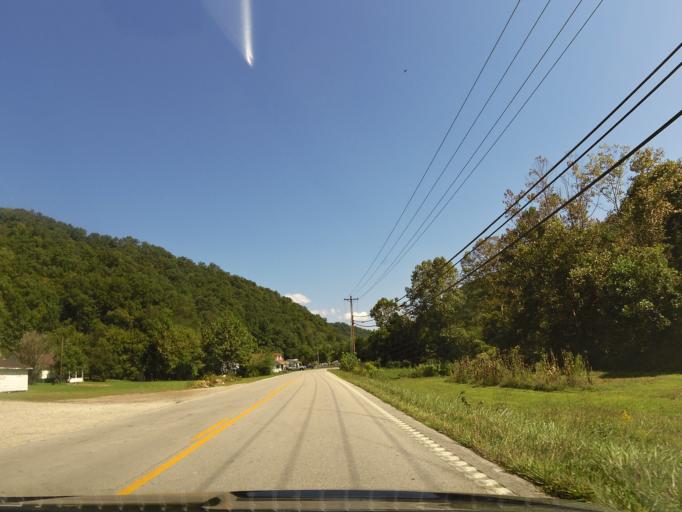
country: US
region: Kentucky
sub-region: Clay County
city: Manchester
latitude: 37.1401
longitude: -83.6114
